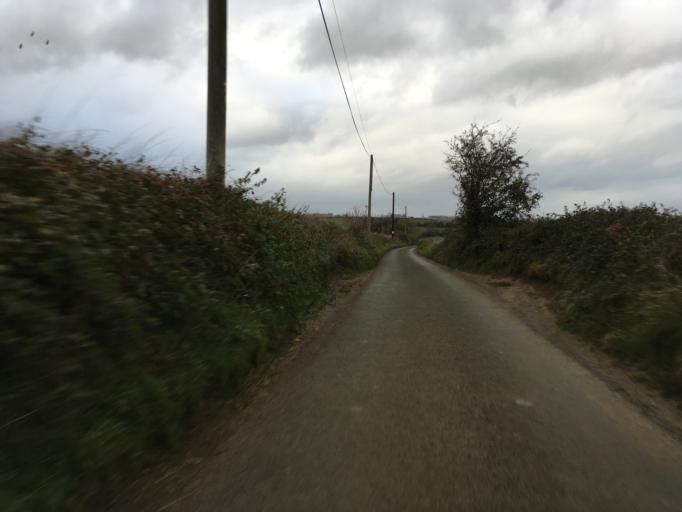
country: GB
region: England
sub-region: South Gloucestershire
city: Marshfield
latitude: 51.4685
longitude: -2.3267
